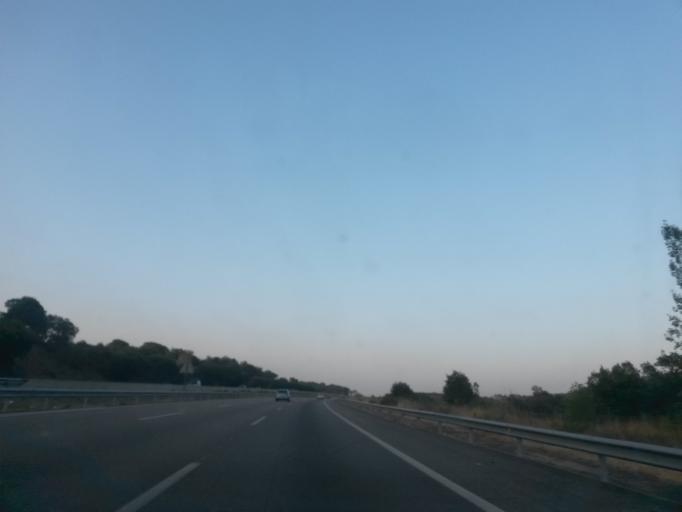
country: ES
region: Catalonia
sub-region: Provincia de Girona
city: Macanet de la Selva
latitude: 41.7588
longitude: 2.7155
